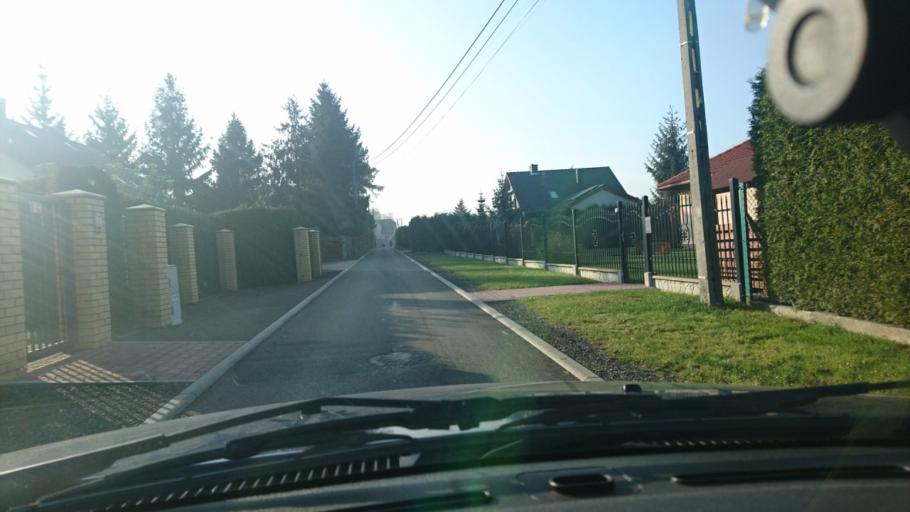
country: PL
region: Silesian Voivodeship
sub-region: Bielsko-Biala
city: Bielsko-Biala
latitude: 49.8490
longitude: 19.0681
